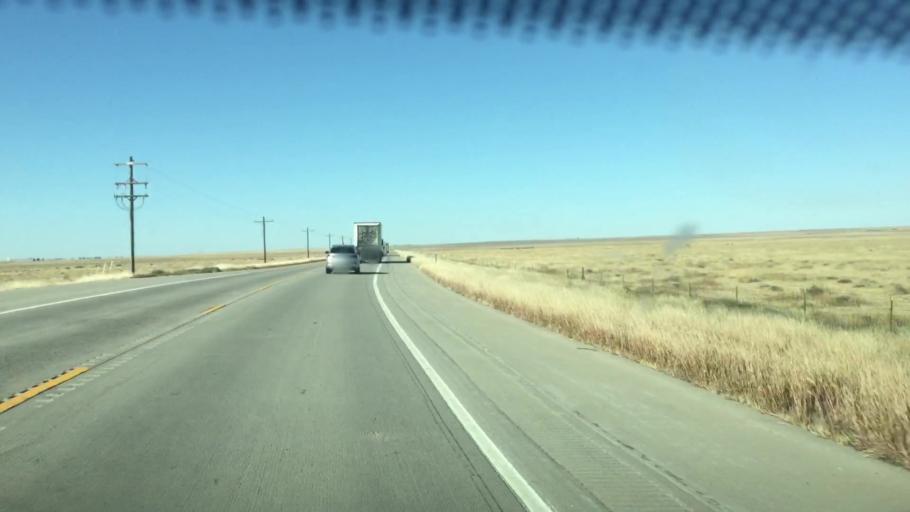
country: US
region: Colorado
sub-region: Kiowa County
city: Eads
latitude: 38.3764
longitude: -102.7301
